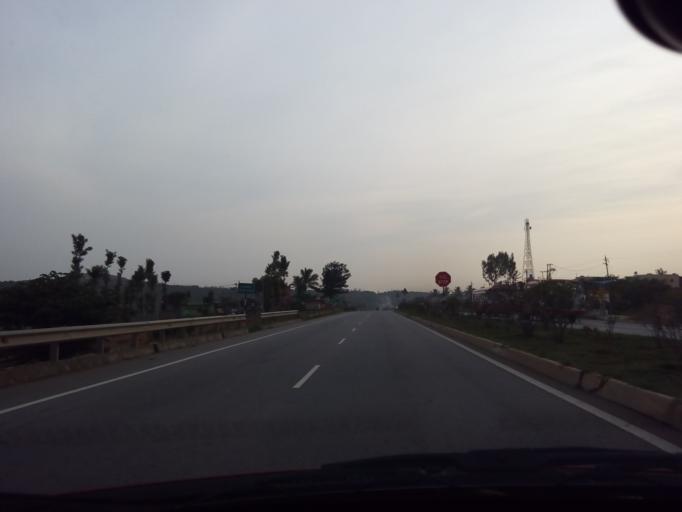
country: IN
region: Karnataka
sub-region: Chikkaballapur
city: Chik Ballapur
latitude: 13.5384
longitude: 77.7688
